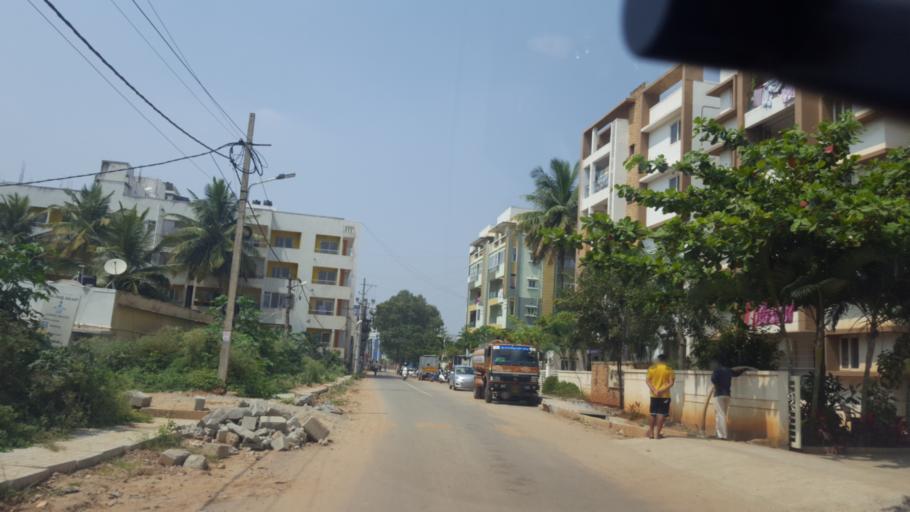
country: IN
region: Karnataka
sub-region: Bangalore Urban
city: Bangalore
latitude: 12.9412
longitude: 77.7034
